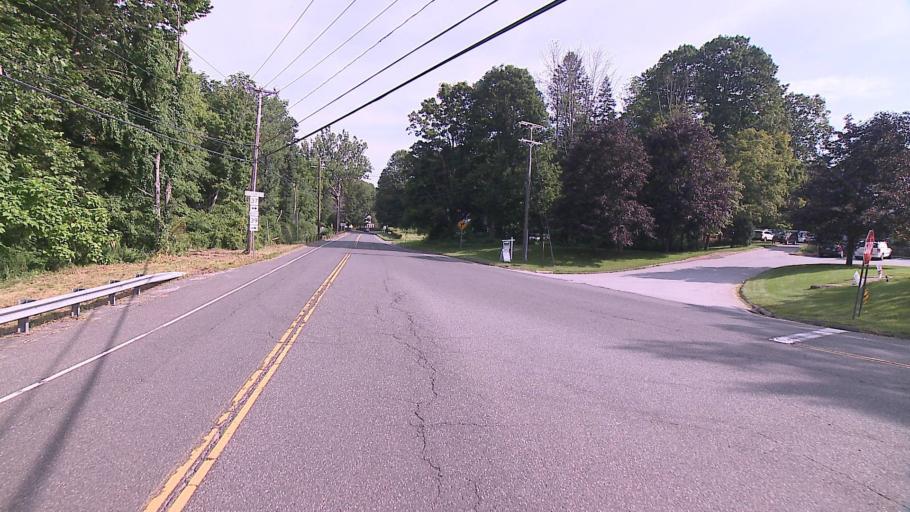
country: US
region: Connecticut
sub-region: Fairfield County
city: Sherman
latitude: 41.5729
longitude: -73.4996
